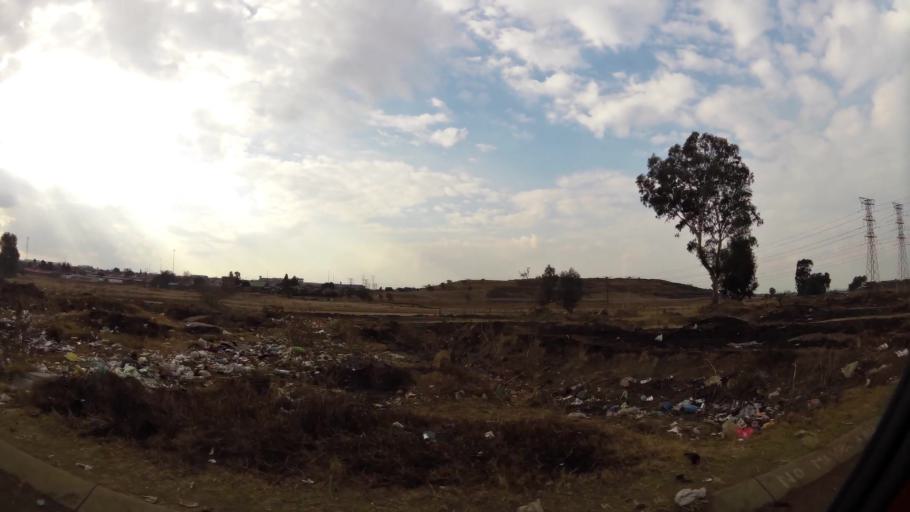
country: ZA
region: Gauteng
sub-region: Sedibeng District Municipality
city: Vanderbijlpark
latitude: -26.6733
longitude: 27.8545
